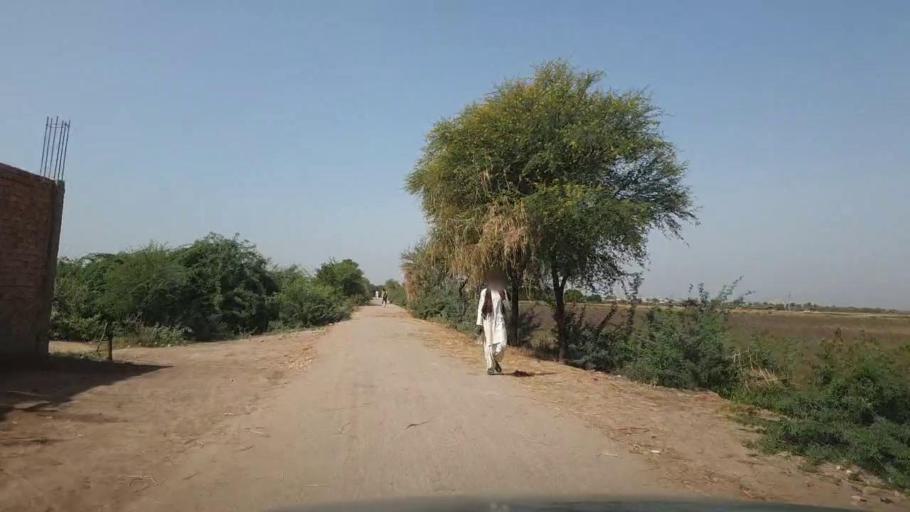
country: PK
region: Sindh
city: Tando Muhammad Khan
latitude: 25.1553
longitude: 68.3985
